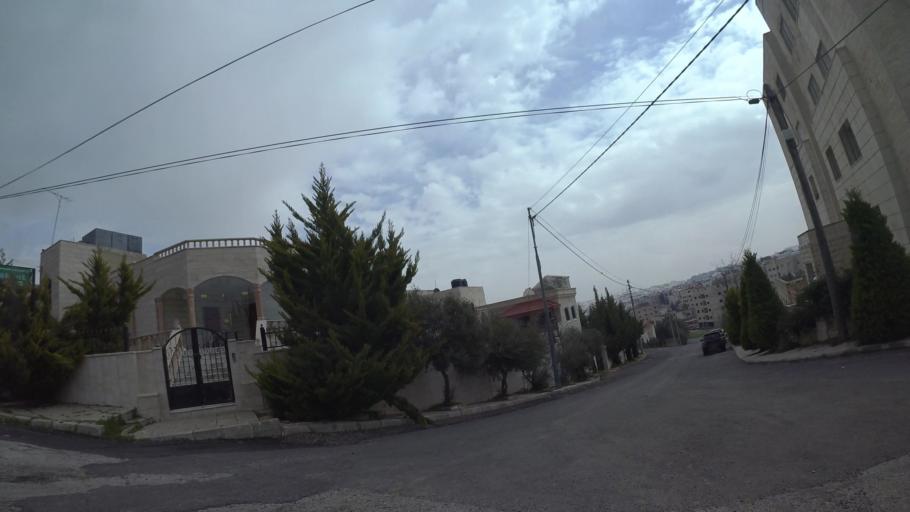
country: JO
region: Amman
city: Umm as Summaq
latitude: 31.9096
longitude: 35.8410
